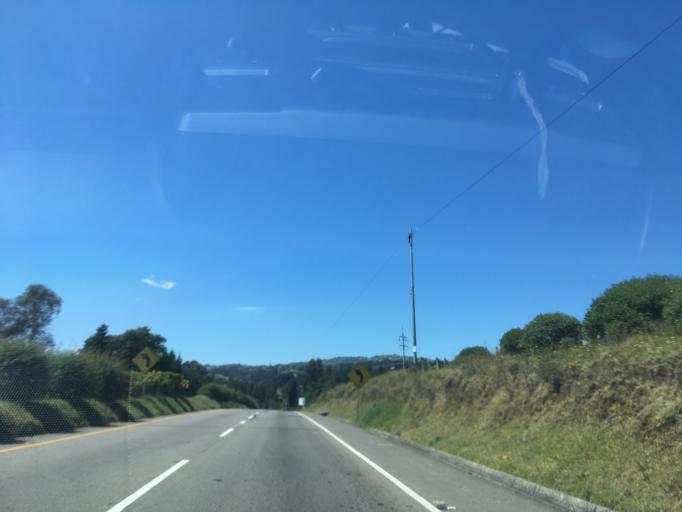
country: CO
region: Boyaca
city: Tuta
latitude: 5.6889
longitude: -73.2601
